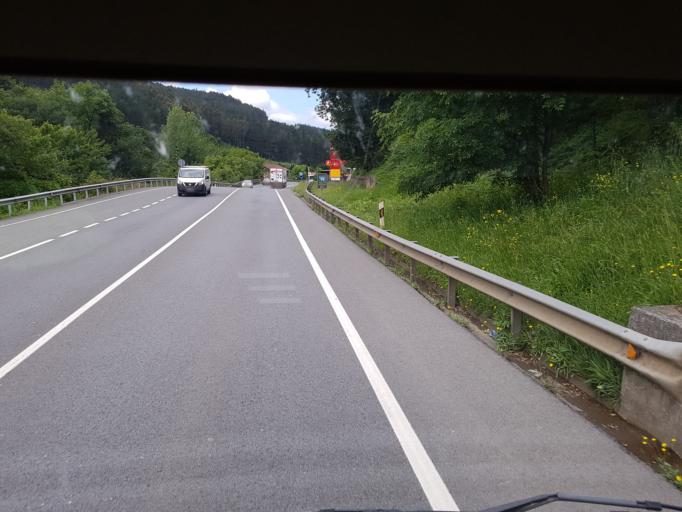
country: ES
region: Basque Country
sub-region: Bizkaia
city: Galdakao
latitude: 43.2312
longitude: -2.7891
